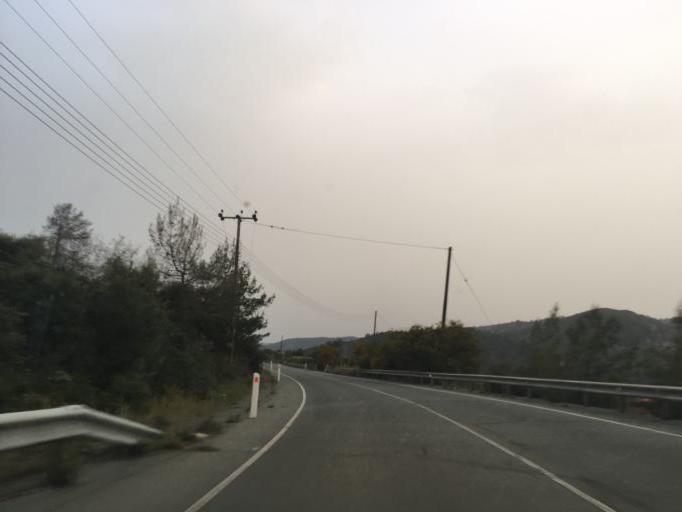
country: CY
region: Limassol
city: Parekklisha
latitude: 34.8065
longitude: 33.1448
